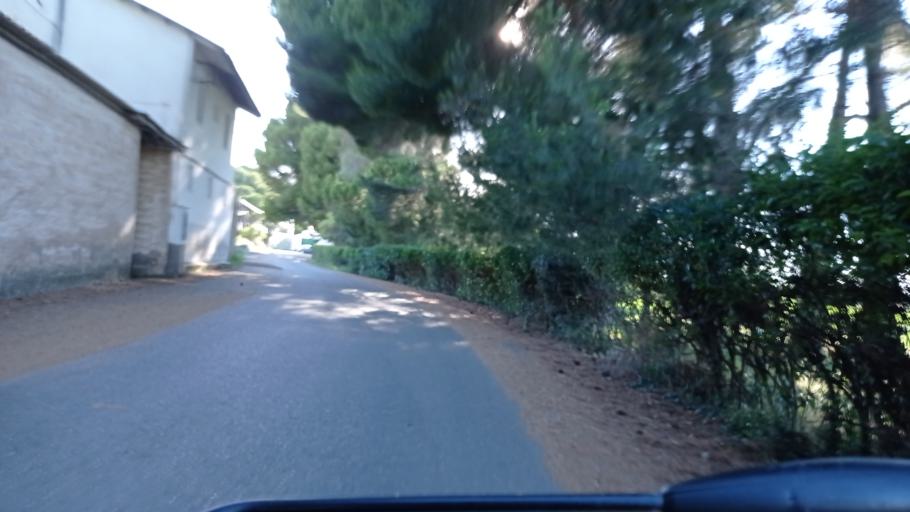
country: ES
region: Aragon
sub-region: Provincia de Zaragoza
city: Oliver-Valdefierro, Oliver, Valdefierro
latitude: 41.6641
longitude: -0.9532
